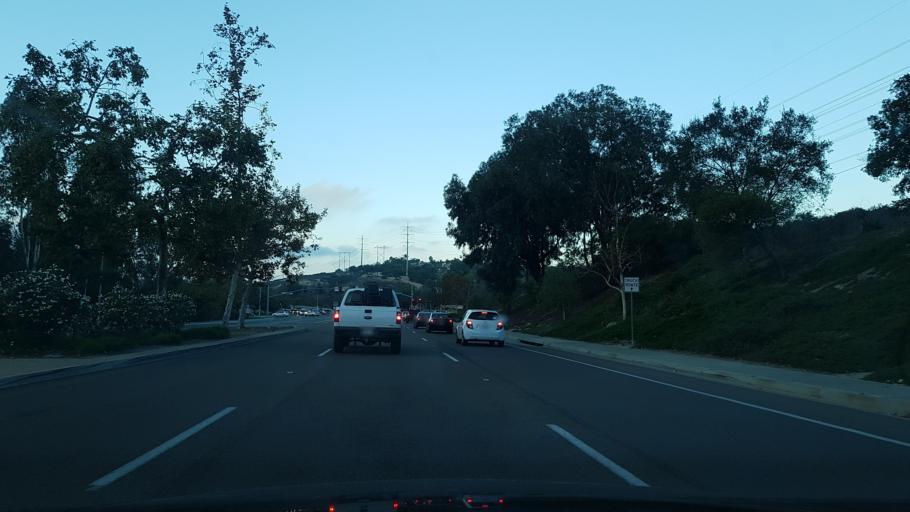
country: US
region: California
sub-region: San Diego County
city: Encinitas
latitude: 33.0714
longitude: -117.2623
